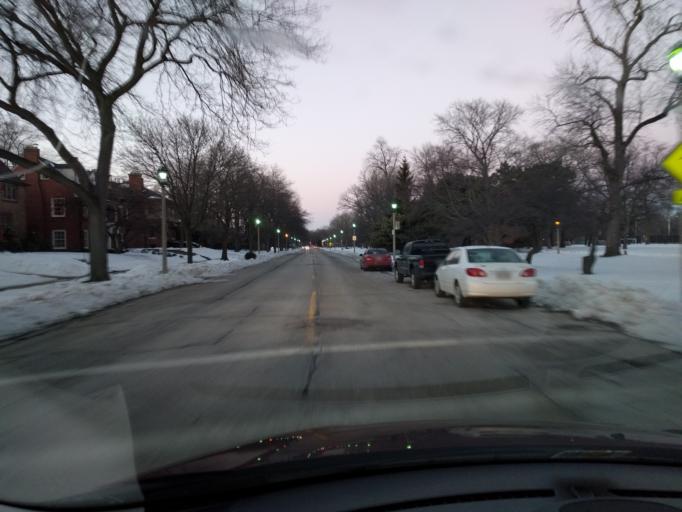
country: US
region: Wisconsin
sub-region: Milwaukee County
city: Shorewood
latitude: 43.0710
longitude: -87.8724
